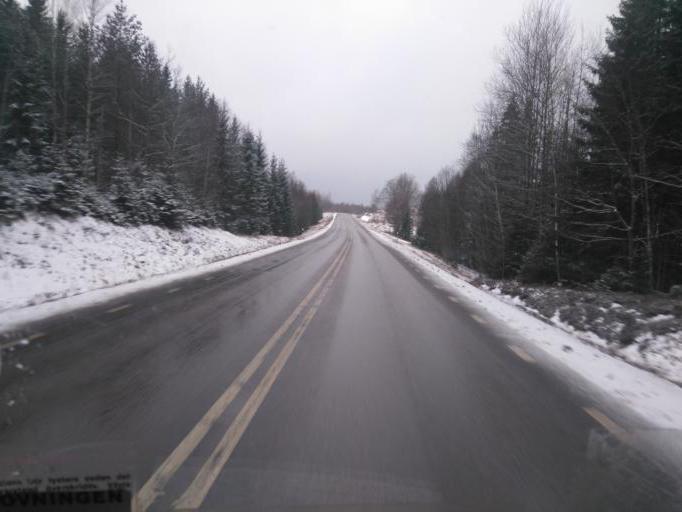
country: SE
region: Joenkoeping
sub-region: Eksjo Kommun
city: Mariannelund
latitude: 57.6363
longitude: 15.6518
